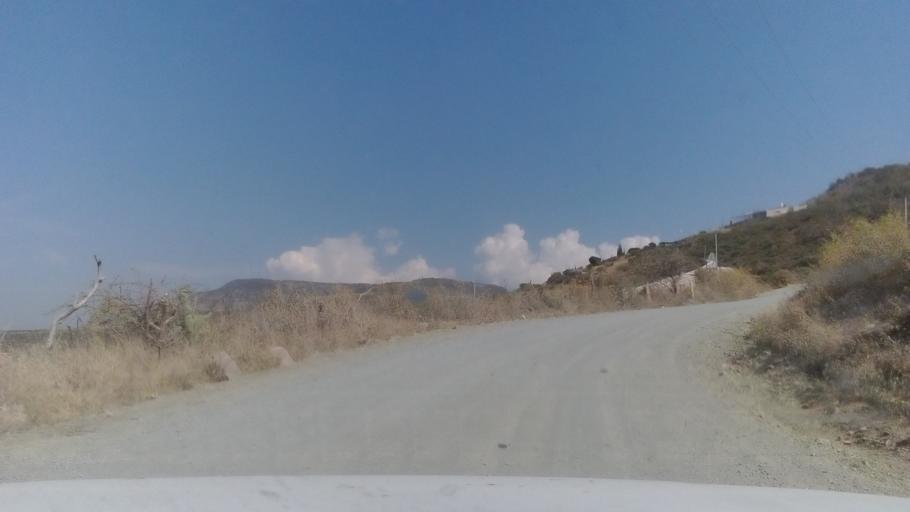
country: MX
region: Guanajuato
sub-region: Leon
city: Medina
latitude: 21.1453
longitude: -101.6029
